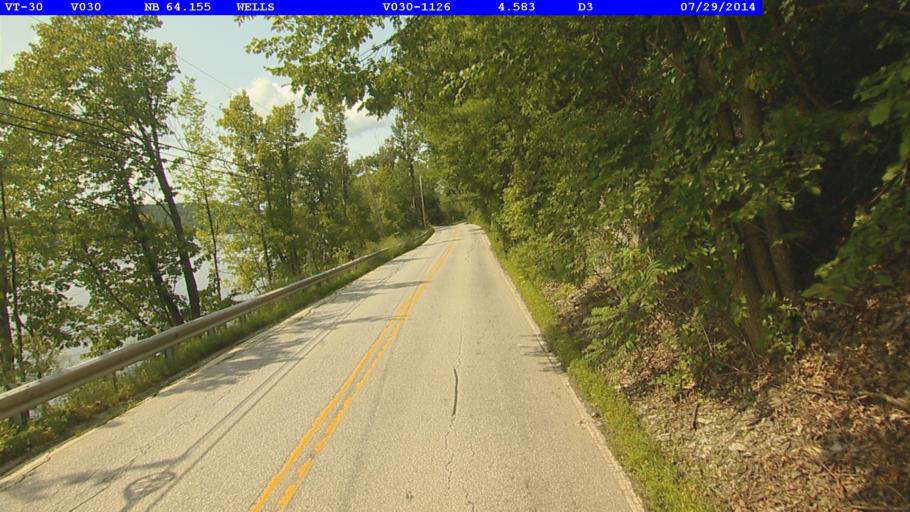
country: US
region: Vermont
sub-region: Rutland County
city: Poultney
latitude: 43.4569
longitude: -73.2051
